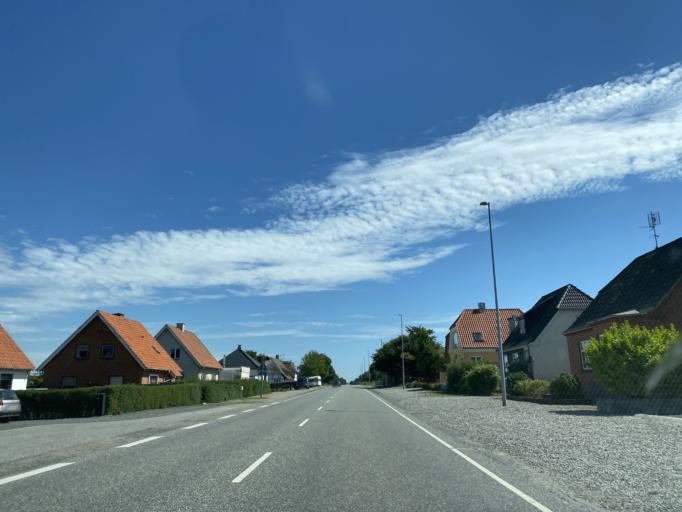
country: DK
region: South Denmark
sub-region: Faaborg-Midtfyn Kommune
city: Faaborg
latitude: 55.1092
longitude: 10.1731
